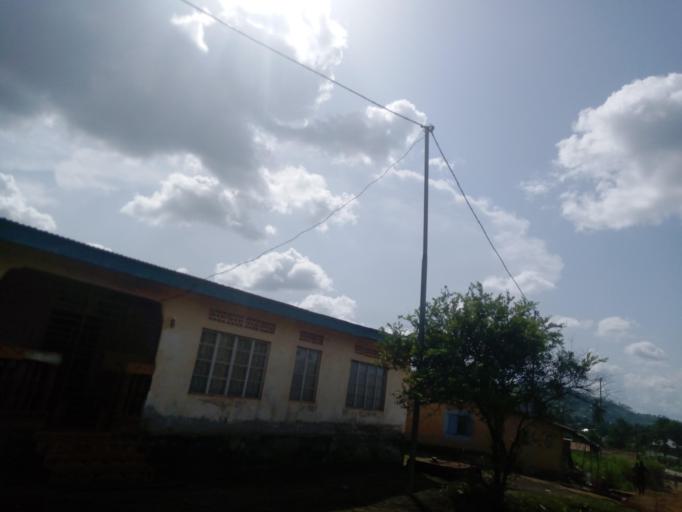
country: SL
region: Northern Province
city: Makeni
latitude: 8.9038
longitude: -12.0327
